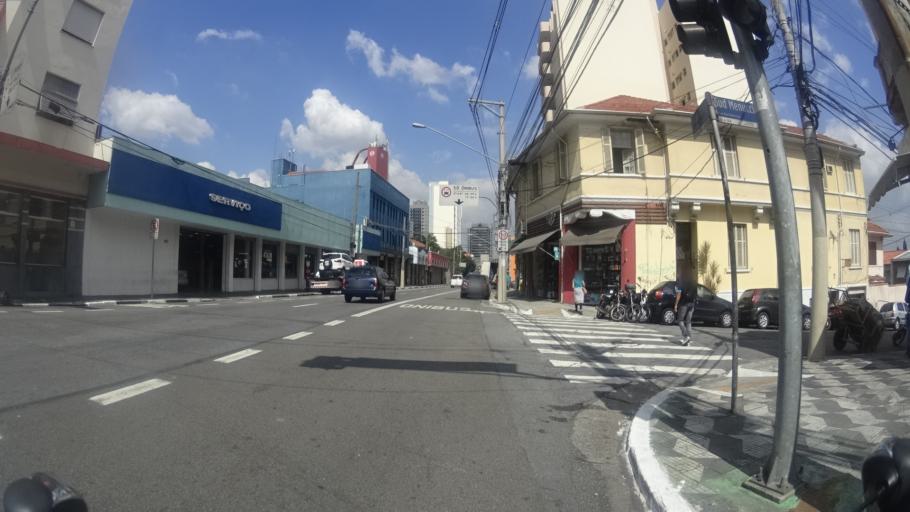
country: BR
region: Sao Paulo
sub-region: Sao Paulo
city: Sao Paulo
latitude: -23.5871
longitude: -46.6357
